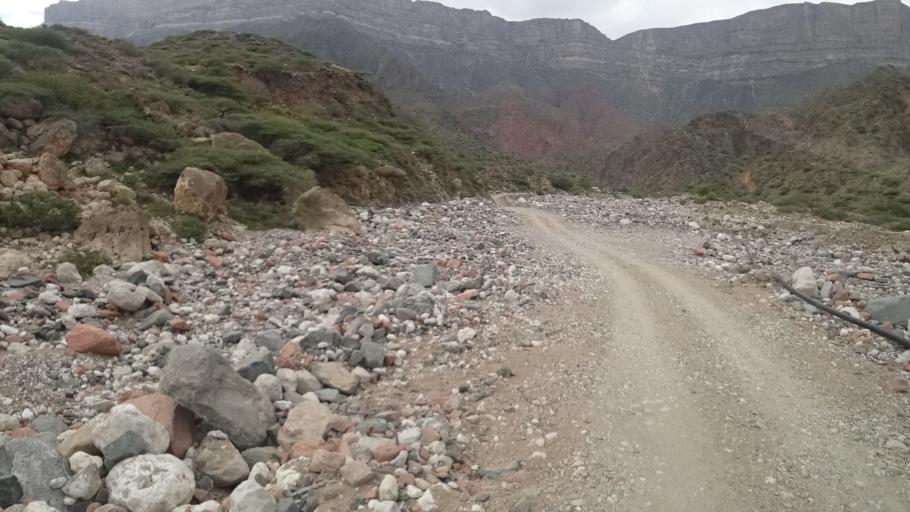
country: OM
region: Zufar
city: Salalah
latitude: 17.1810
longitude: 54.9466
